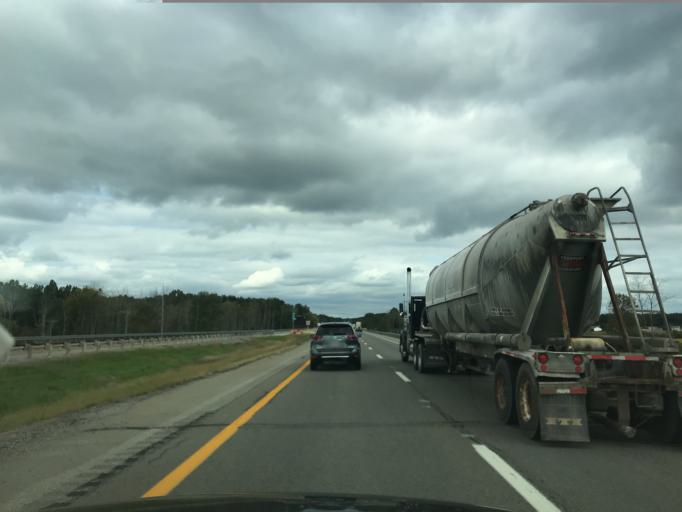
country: US
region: Ohio
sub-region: Mahoning County
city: Boardman
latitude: 40.9879
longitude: -80.6879
